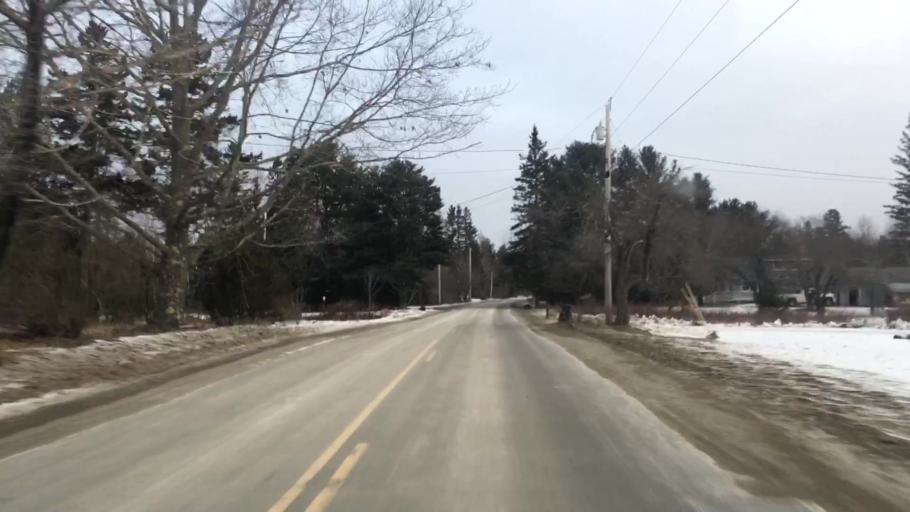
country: US
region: Maine
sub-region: Hancock County
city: Franklin
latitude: 44.6881
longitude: -68.3494
